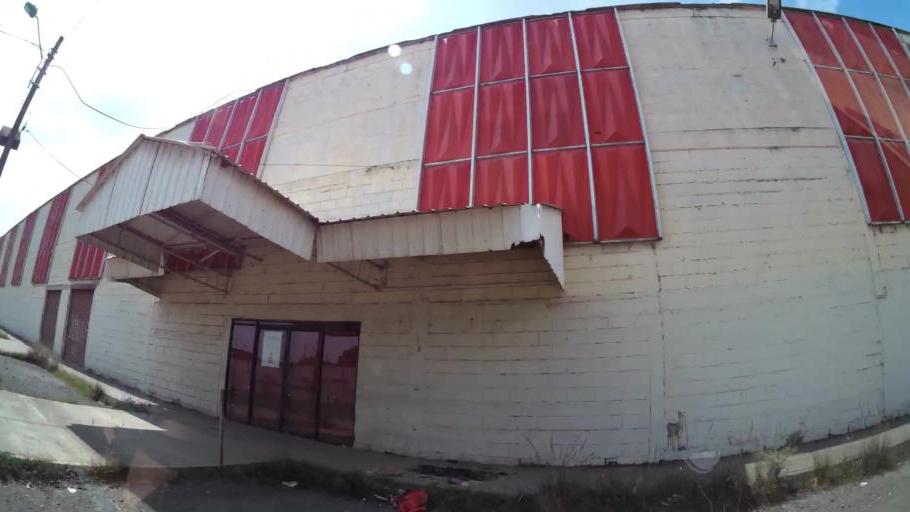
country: CO
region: Valle del Cauca
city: Cali
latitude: 3.4957
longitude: -76.5097
